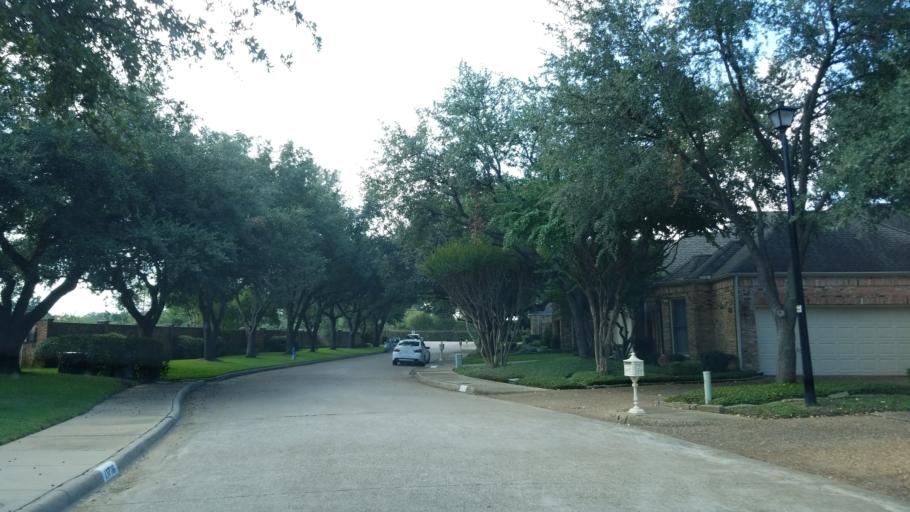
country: US
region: Texas
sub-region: Dallas County
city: Addison
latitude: 32.9344
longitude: -96.7894
